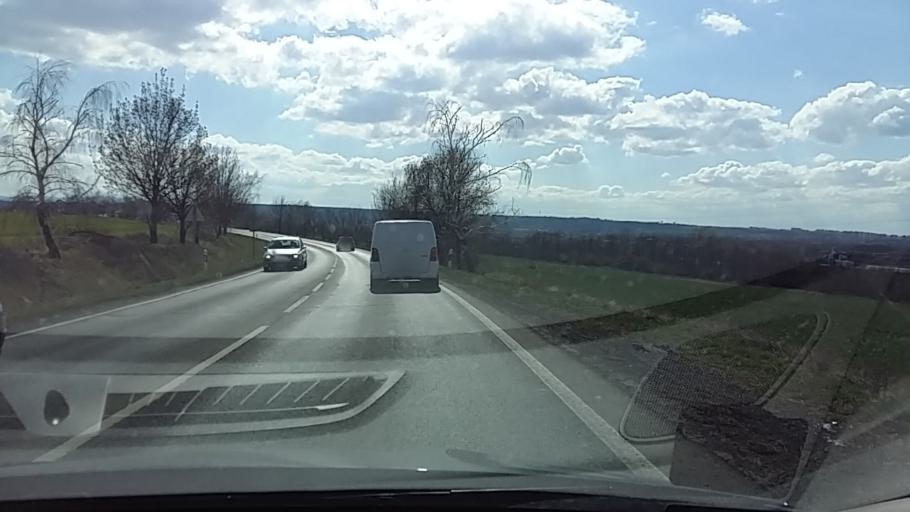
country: HU
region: Baranya
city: Kozarmisleny
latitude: 46.0627
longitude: 18.2743
